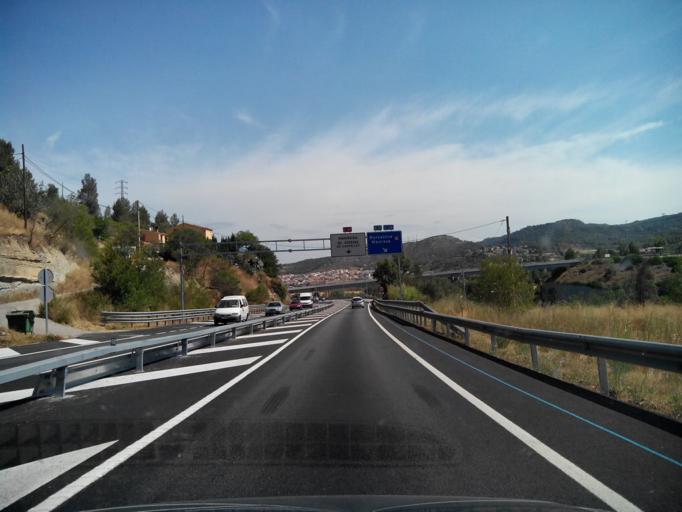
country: ES
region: Catalonia
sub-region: Provincia de Barcelona
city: Monistrol de Montserrat
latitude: 41.6473
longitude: 1.8572
